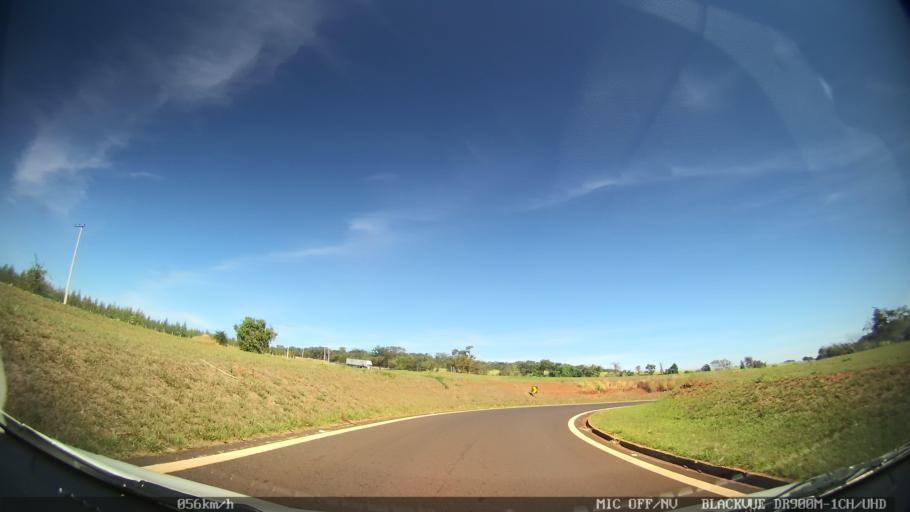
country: BR
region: Sao Paulo
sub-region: Sao Simao
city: Sao Simao
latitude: -21.5290
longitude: -47.6413
